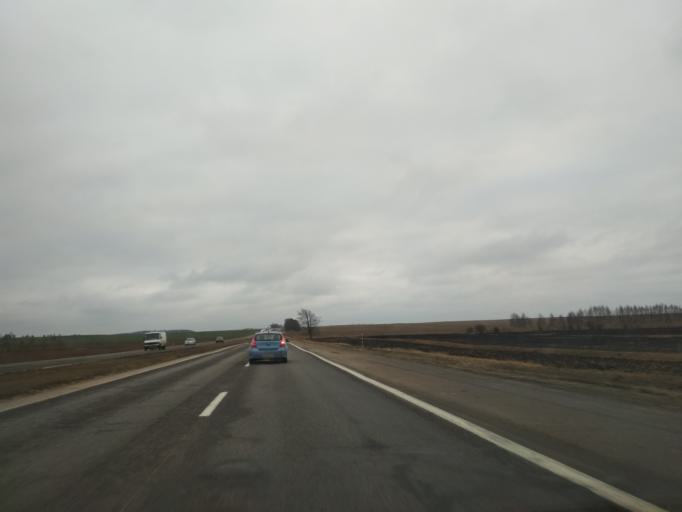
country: BY
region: Minsk
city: Blon'
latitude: 53.5595
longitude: 28.1489
